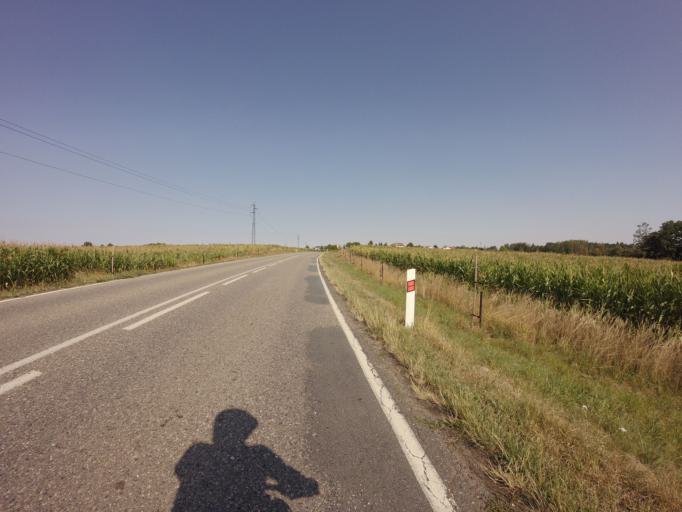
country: CZ
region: Central Bohemia
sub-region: Okres Benesov
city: Benesov
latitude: 49.7971
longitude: 14.6581
